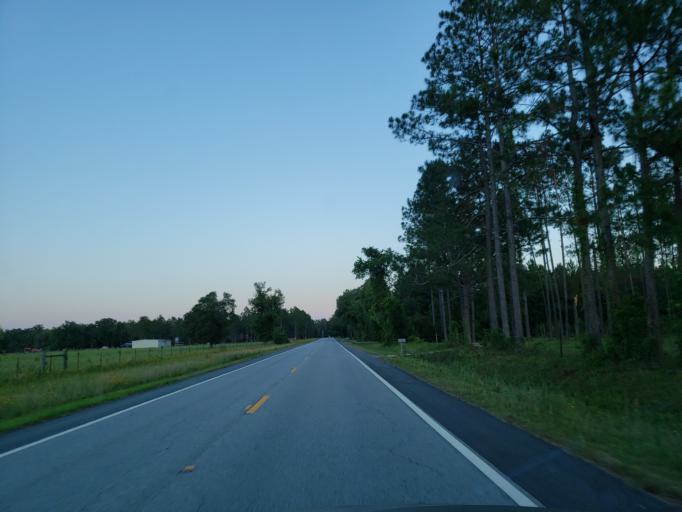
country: US
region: Florida
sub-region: Hamilton County
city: Jasper
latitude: 30.5540
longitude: -83.0721
